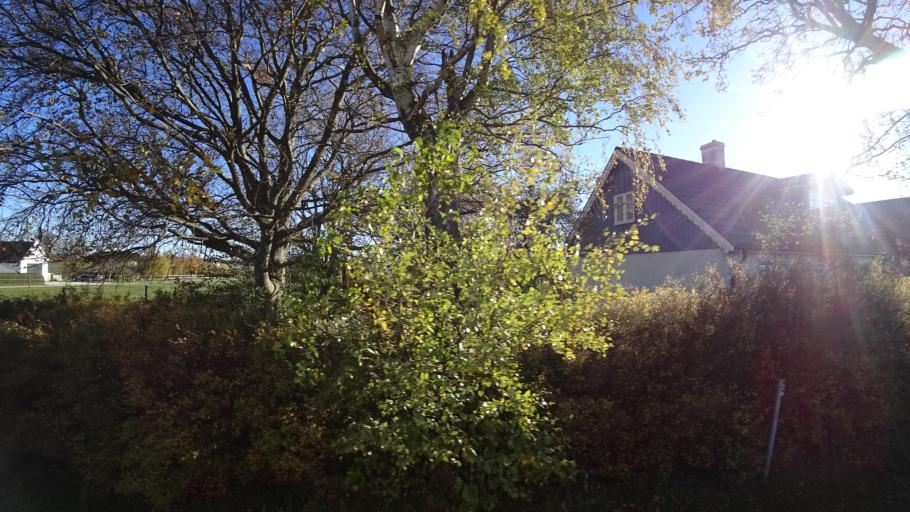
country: SE
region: Skane
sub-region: Svedala Kommun
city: Klagerup
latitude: 55.6480
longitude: 13.2896
